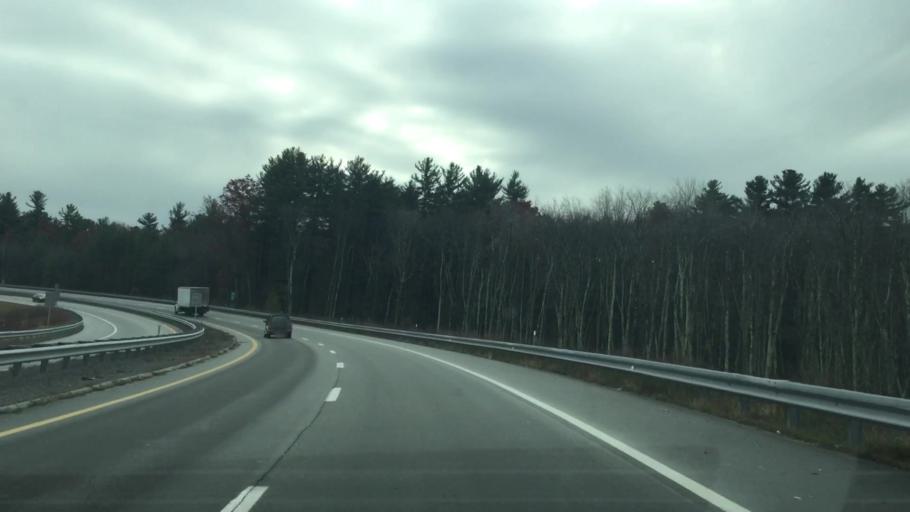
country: US
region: New Hampshire
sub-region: Rockingham County
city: Salem
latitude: 42.7587
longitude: -71.2339
